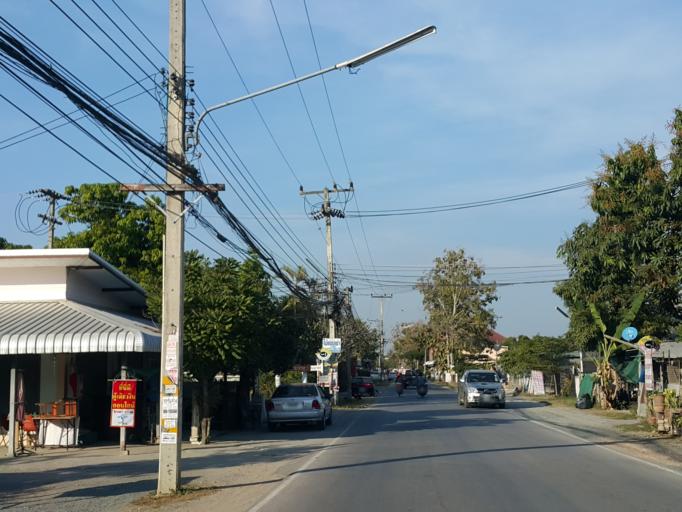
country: TH
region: Chiang Mai
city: San Sai
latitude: 18.7995
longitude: 99.0603
